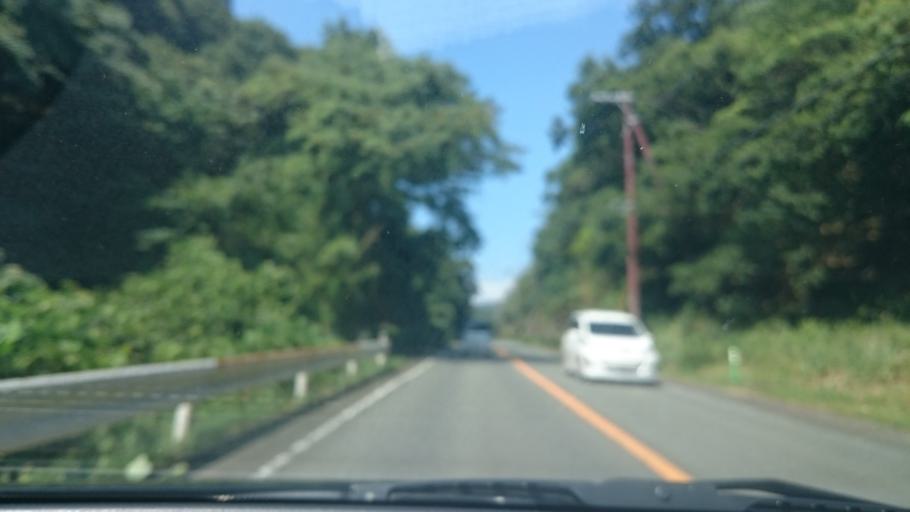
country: JP
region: Shizuoka
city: Heda
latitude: 34.7945
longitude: 138.7645
